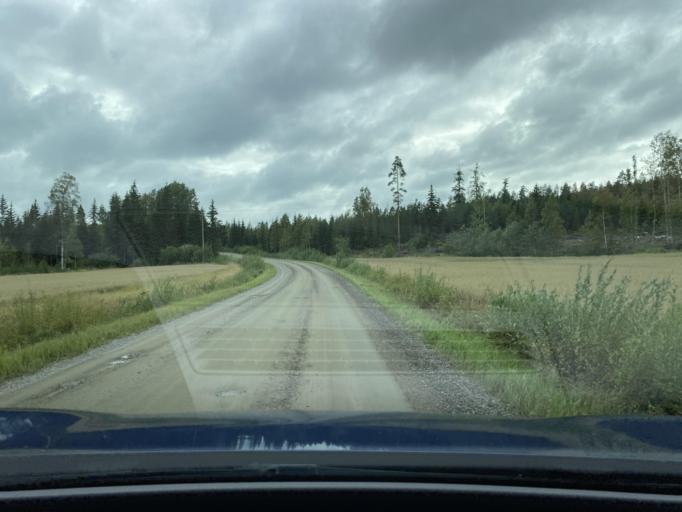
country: FI
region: Pirkanmaa
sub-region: Lounais-Pirkanmaa
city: Punkalaidun
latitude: 61.2141
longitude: 23.1689
